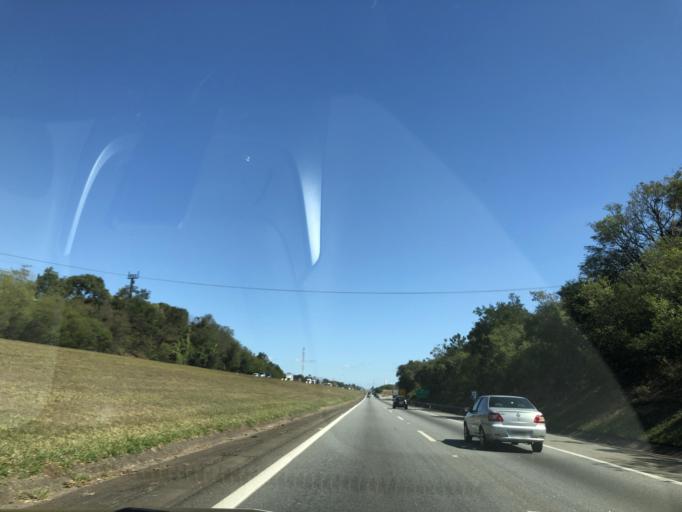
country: BR
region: Sao Paulo
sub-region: Sorocaba
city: Sorocaba
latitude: -23.4232
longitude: -47.3564
